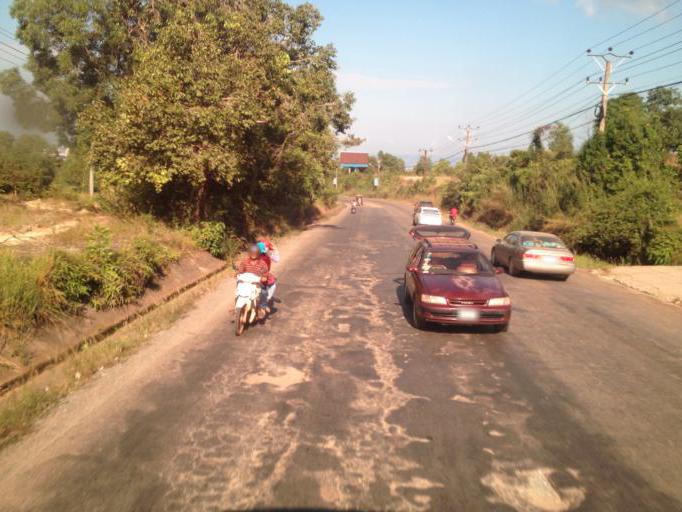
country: KH
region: Preah Sihanouk
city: Sihanoukville
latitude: 10.6405
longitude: 103.5291
